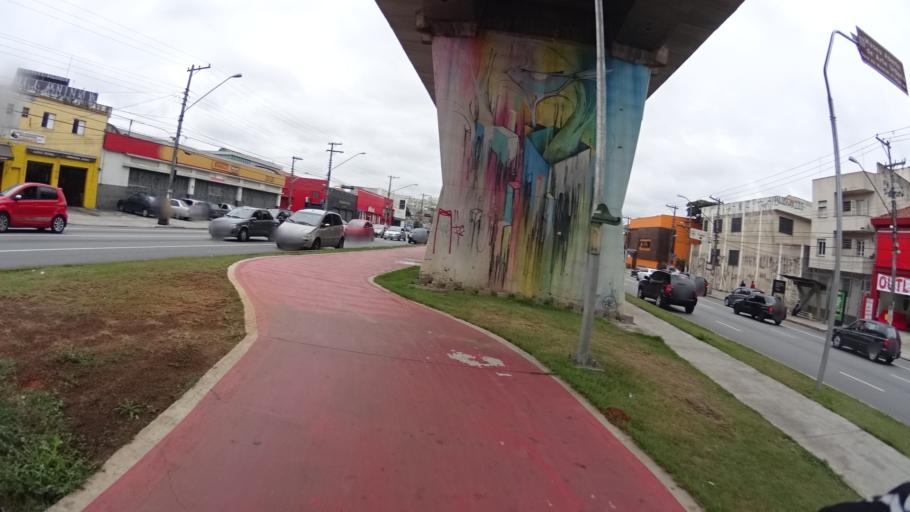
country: BR
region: Sao Paulo
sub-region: Sao Paulo
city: Sao Paulo
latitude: -23.5130
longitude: -46.6250
